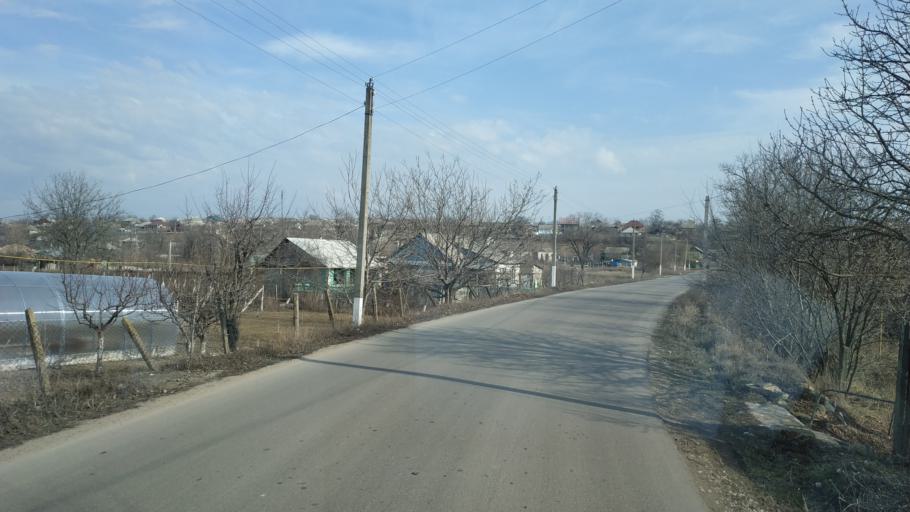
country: MD
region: Anenii Noi
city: Anenii Noi
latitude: 46.9201
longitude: 29.1043
